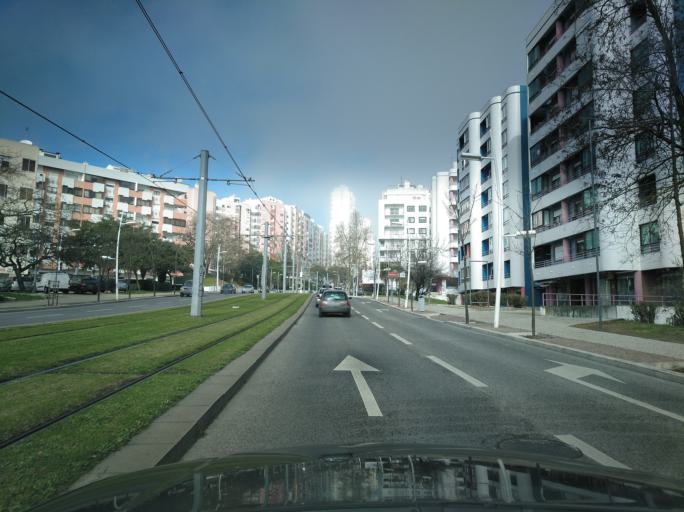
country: PT
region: Setubal
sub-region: Almada
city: Pragal
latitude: 38.6712
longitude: -9.1662
